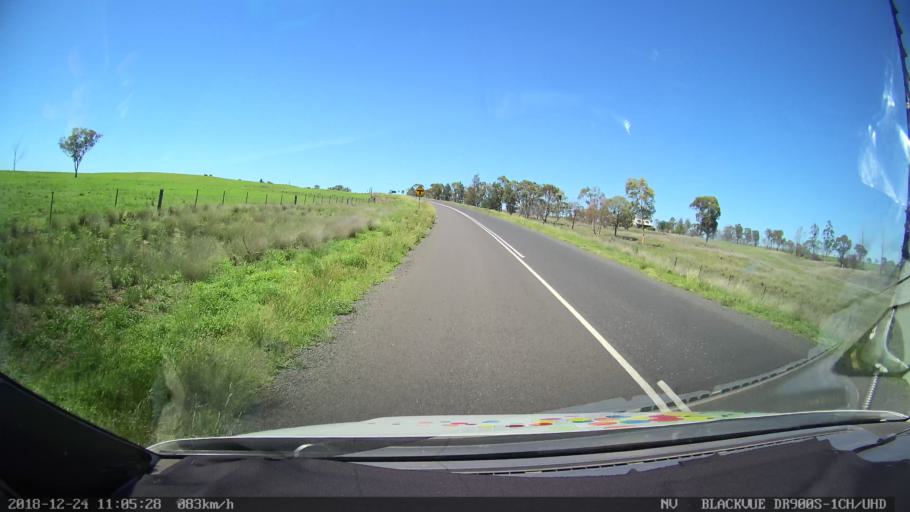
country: AU
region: New South Wales
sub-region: Upper Hunter Shire
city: Merriwa
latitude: -32.1209
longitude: 150.3711
